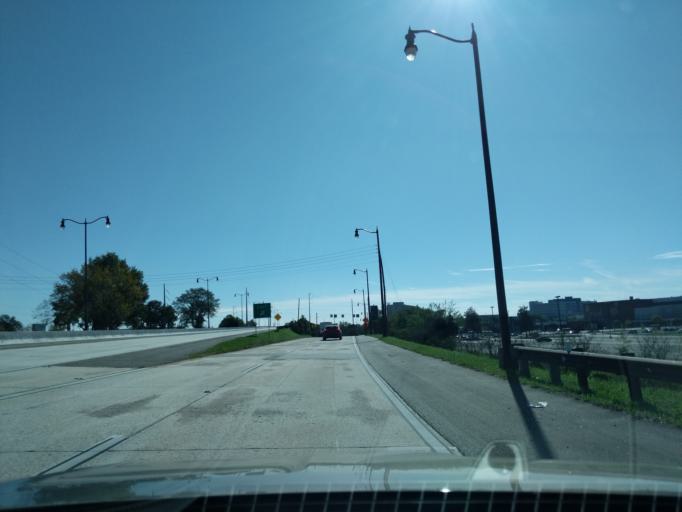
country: US
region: Georgia
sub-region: Richmond County
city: Augusta
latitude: 33.4790
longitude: -81.9872
